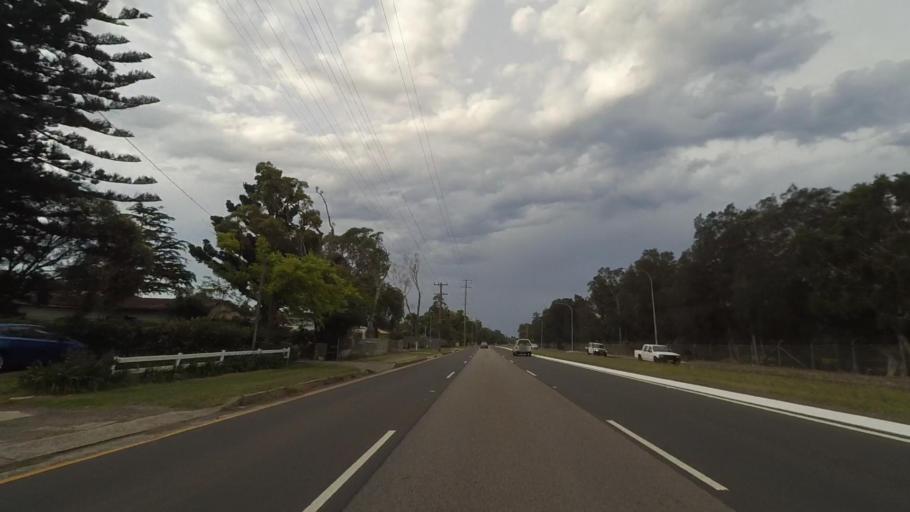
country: AU
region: New South Wales
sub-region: Wollongong
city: Lake Heights
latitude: -34.5158
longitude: 150.8727
